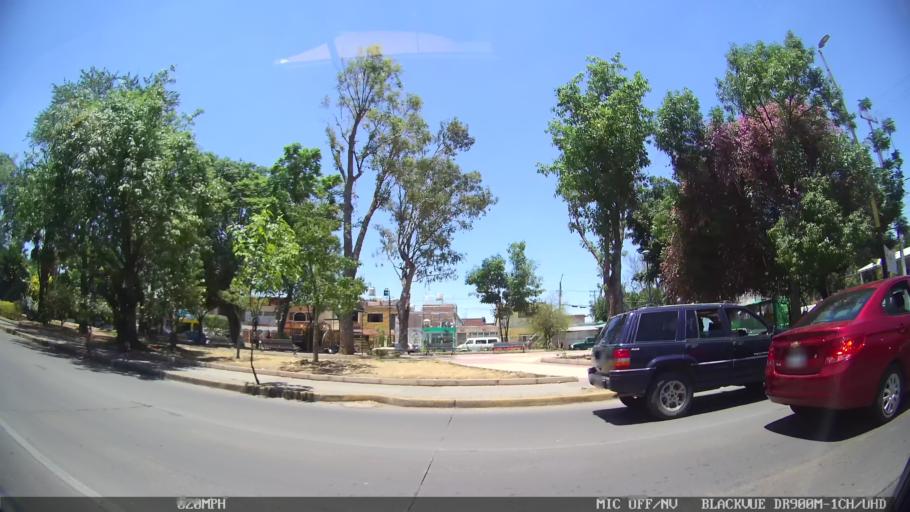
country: MX
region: Jalisco
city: Tlaquepaque
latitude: 20.6622
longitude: -103.2827
